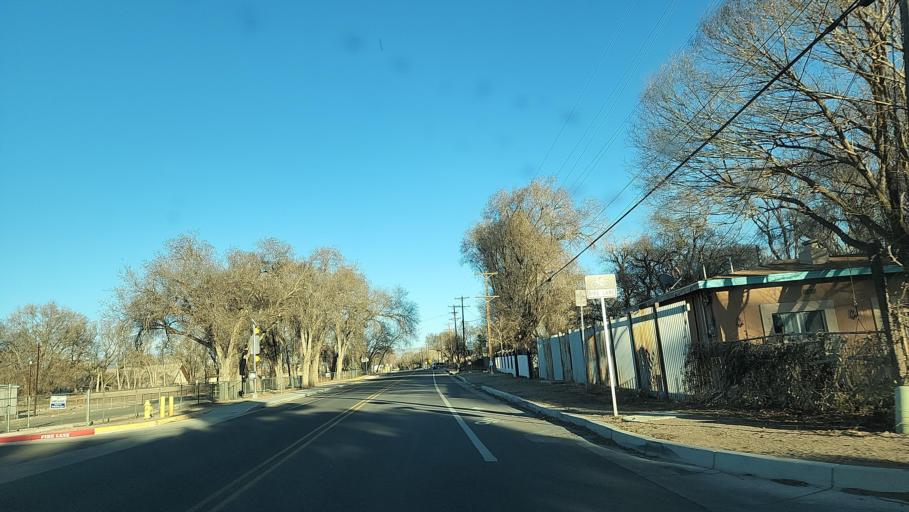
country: US
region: New Mexico
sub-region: Bernalillo County
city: South Valley
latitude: 35.0306
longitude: -106.6927
